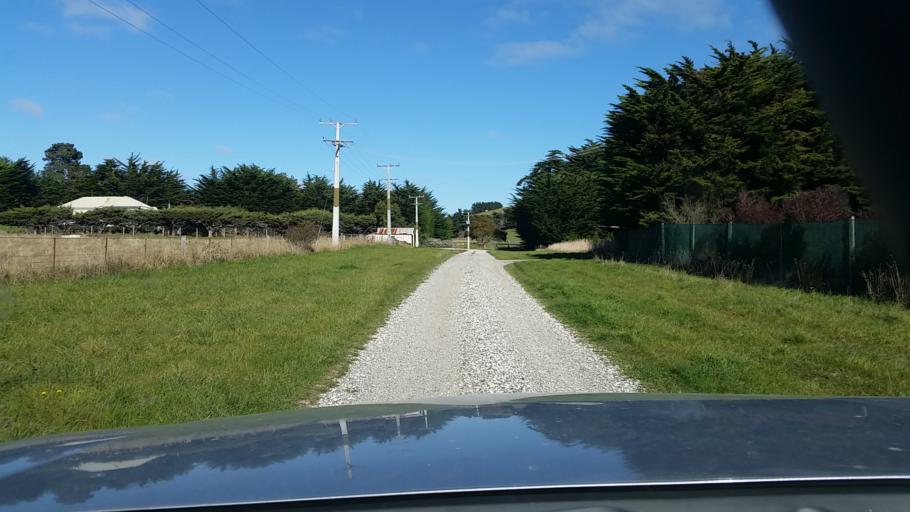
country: NZ
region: Marlborough
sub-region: Marlborough District
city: Blenheim
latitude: -41.7404
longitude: 174.1667
